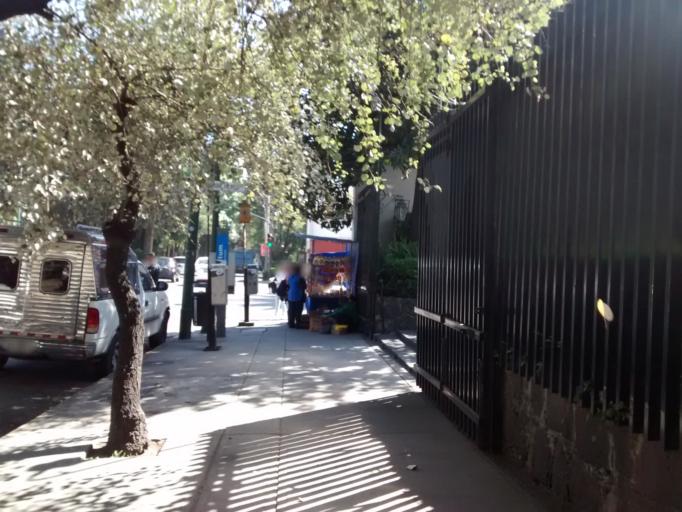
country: MX
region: Mexico City
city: Miguel Hidalgo
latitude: 19.4343
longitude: -99.2020
